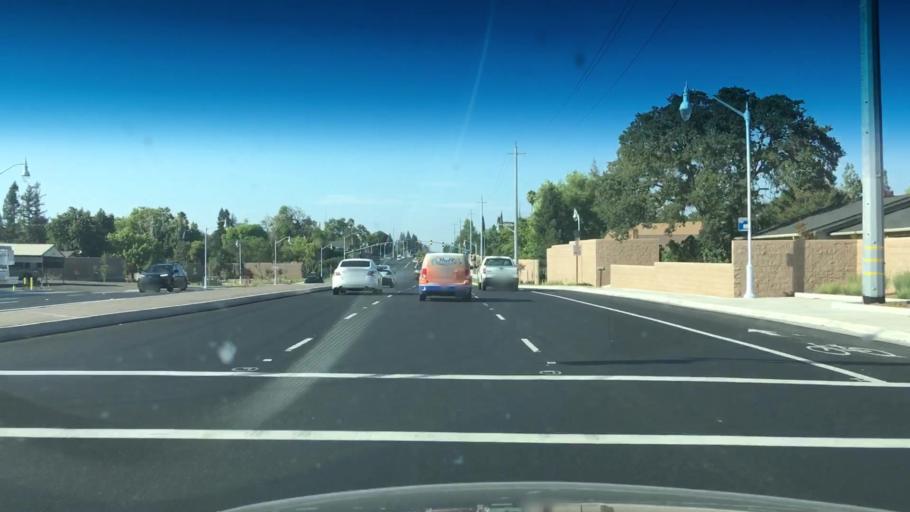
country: US
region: California
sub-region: Sacramento County
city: Gold River
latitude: 38.6462
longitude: -121.2254
